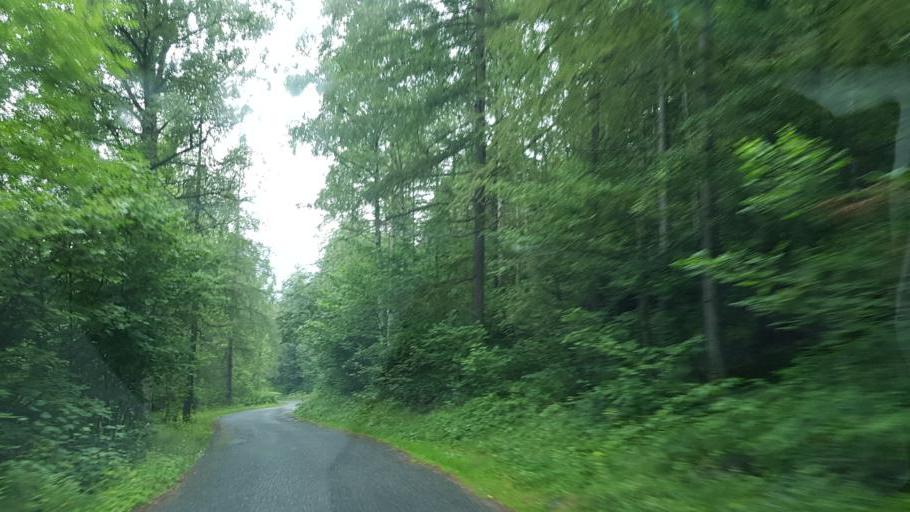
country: IT
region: Piedmont
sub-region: Provincia di Cuneo
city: Sampeyre
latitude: 44.5665
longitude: 7.1768
